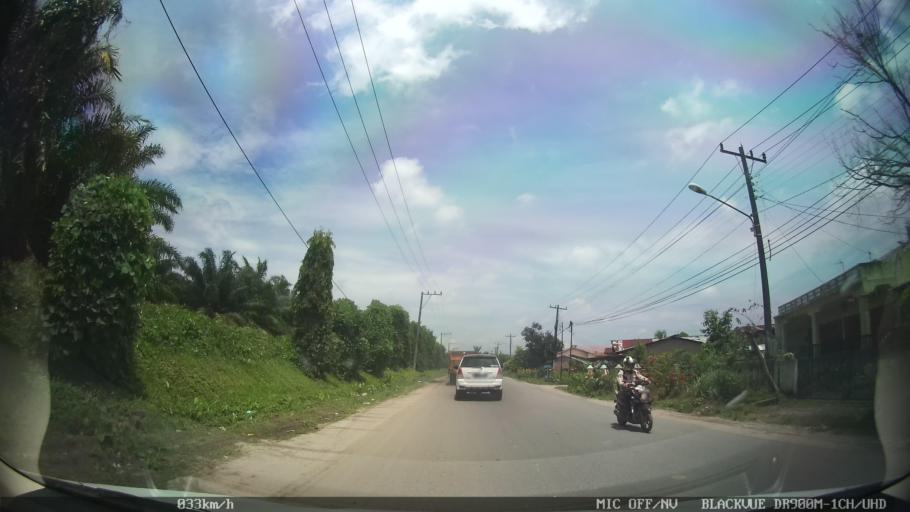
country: ID
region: North Sumatra
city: Perbaungan
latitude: 3.5358
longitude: 98.8845
